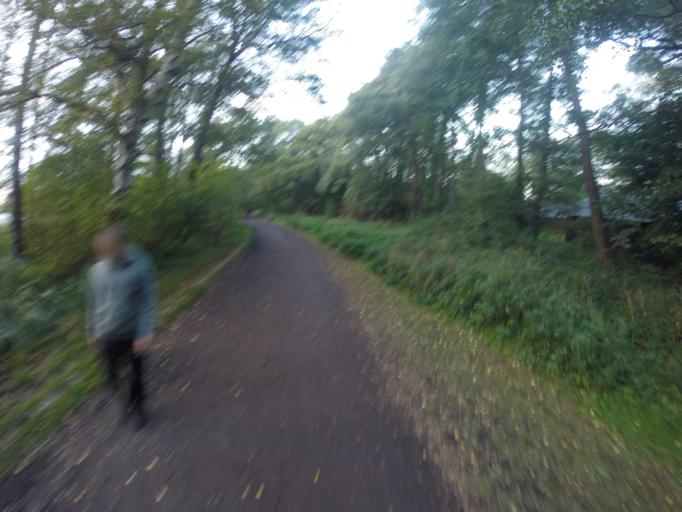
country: DK
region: Capital Region
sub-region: Gladsaxe Municipality
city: Buddinge
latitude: 55.7675
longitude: 12.4714
